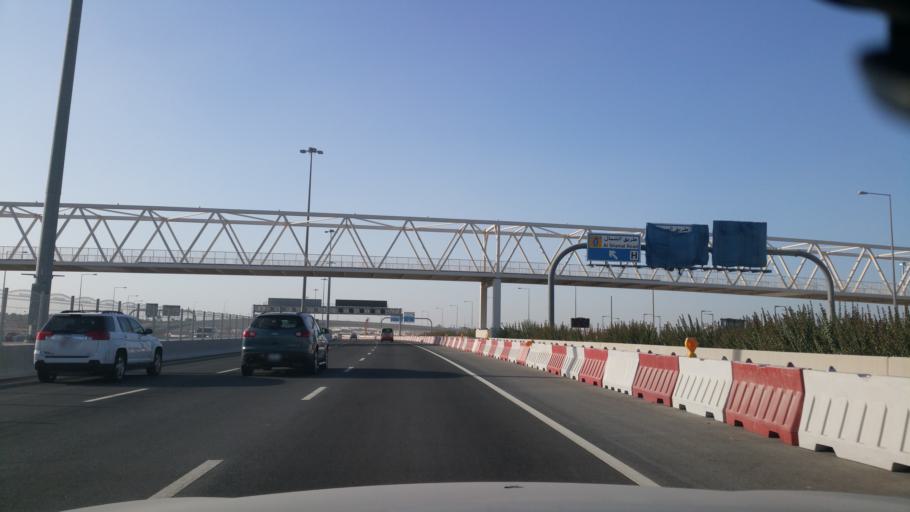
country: QA
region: Baladiyat ad Dawhah
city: Doha
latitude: 25.2306
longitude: 51.5308
